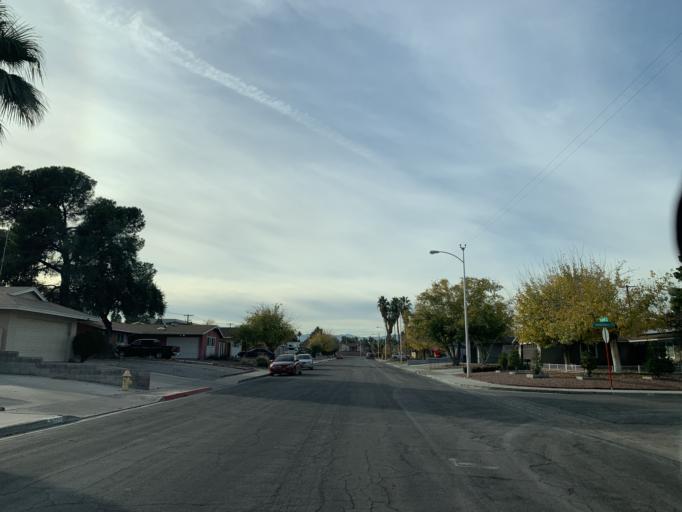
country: US
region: Nevada
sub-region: Clark County
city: Las Vegas
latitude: 36.1475
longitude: -115.1701
